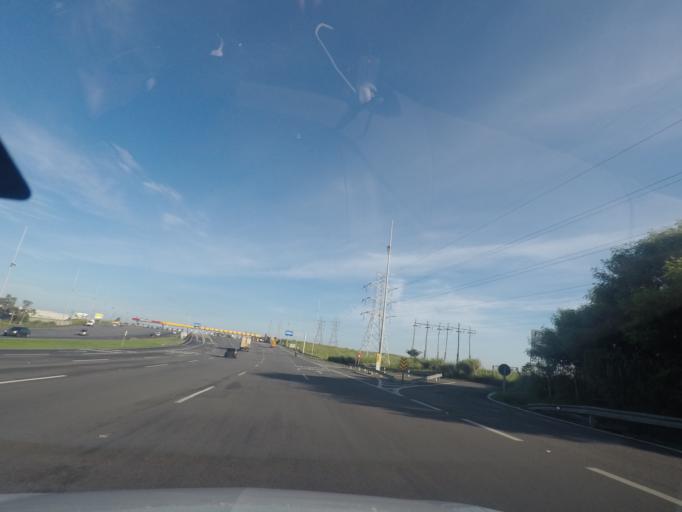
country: BR
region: Sao Paulo
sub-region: Sumare
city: Sumare
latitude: -22.7734
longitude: -47.2356
